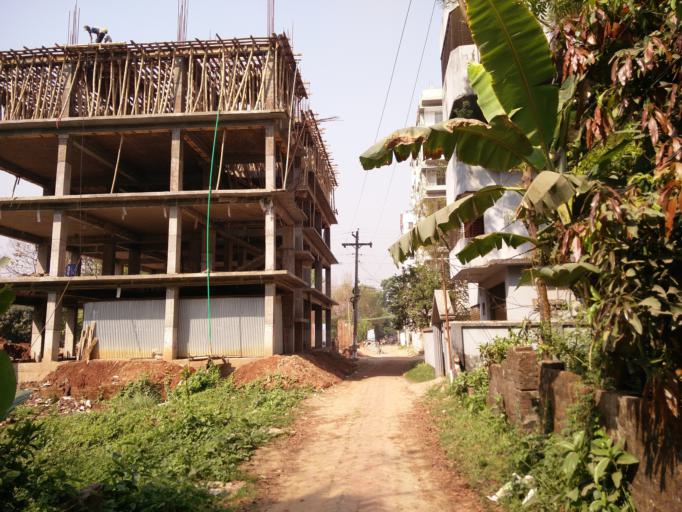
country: BD
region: Dhaka
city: Tungi
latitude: 23.8576
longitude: 90.2553
